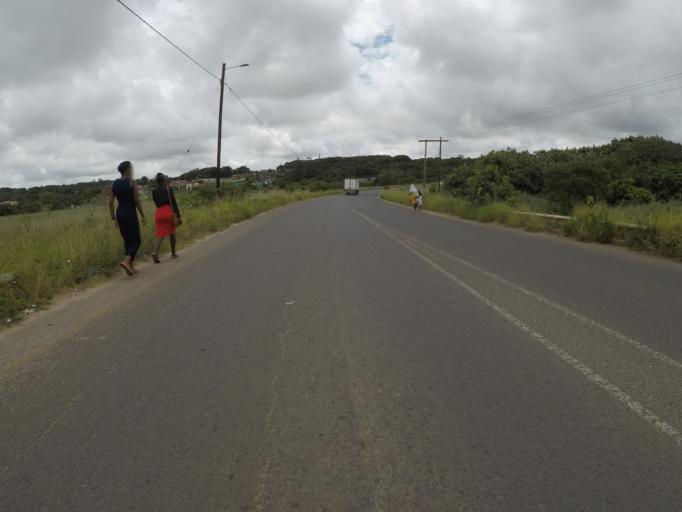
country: ZA
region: KwaZulu-Natal
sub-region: uThungulu District Municipality
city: eSikhawini
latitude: -28.8563
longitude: 31.9230
